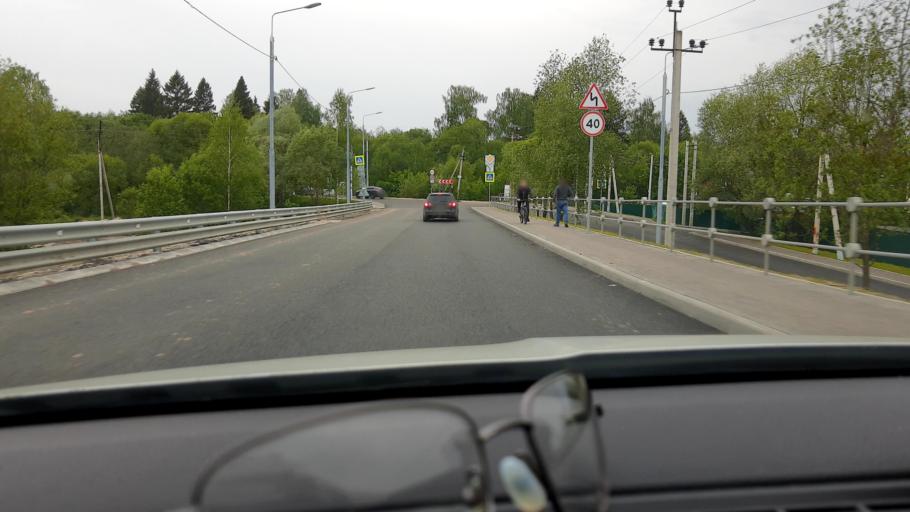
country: RU
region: Moskovskaya
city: Vatutinki
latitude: 55.5170
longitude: 37.3302
